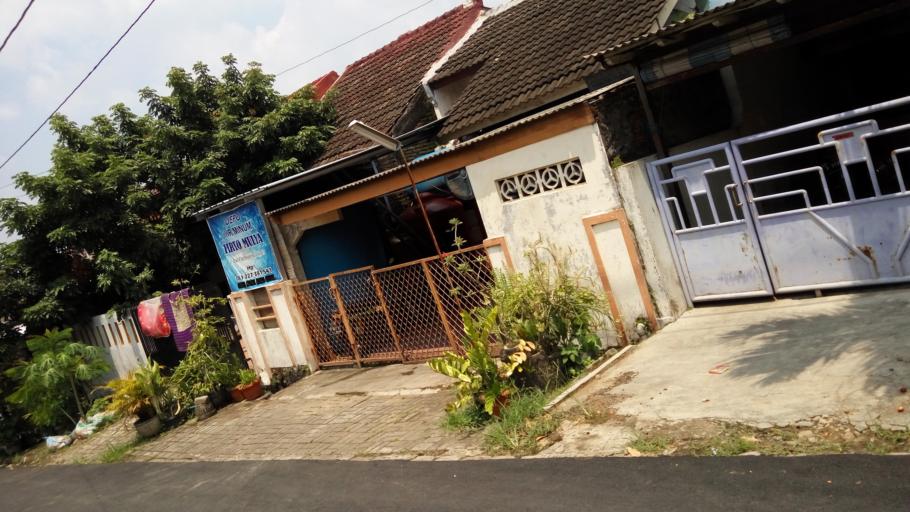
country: ID
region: Central Java
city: Mranggen
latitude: -7.0425
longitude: 110.4732
